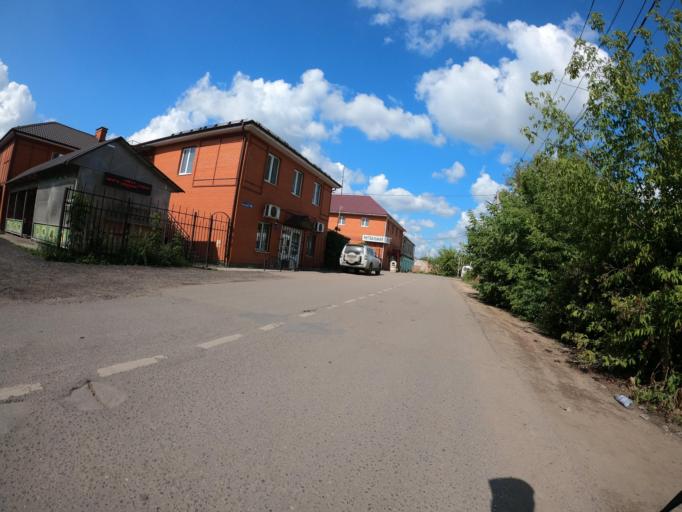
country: RU
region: Moskovskaya
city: Lopatinskiy
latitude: 55.3121
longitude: 38.7002
